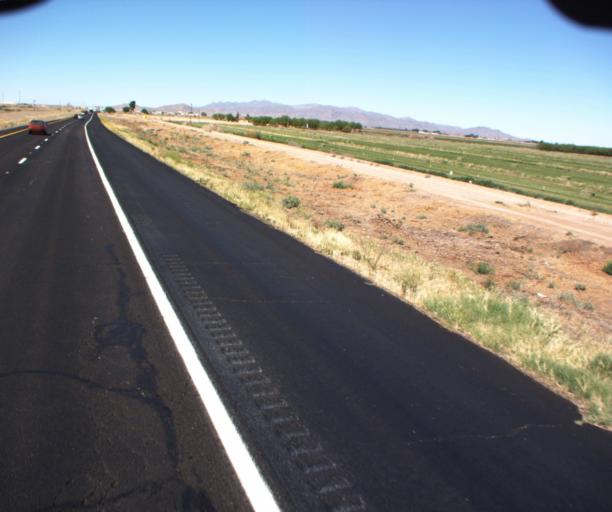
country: US
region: Arizona
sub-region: Maricopa County
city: Buckeye
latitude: 33.3486
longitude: -112.6243
